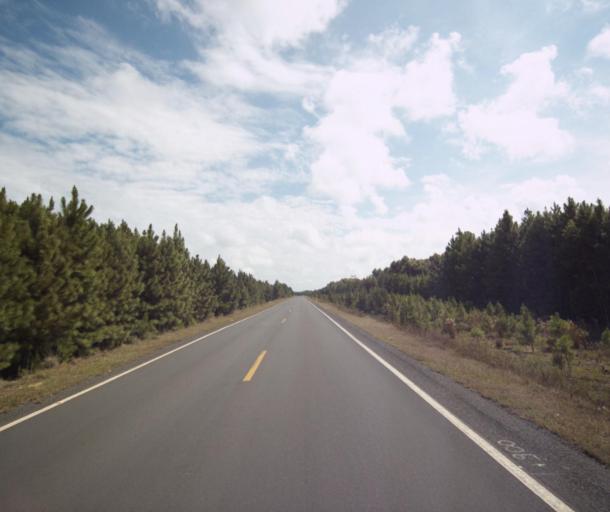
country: BR
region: Rio Grande do Sul
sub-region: Sao Lourenco Do Sul
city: Sao Lourenco do Sul
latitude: -31.4582
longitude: -51.2235
